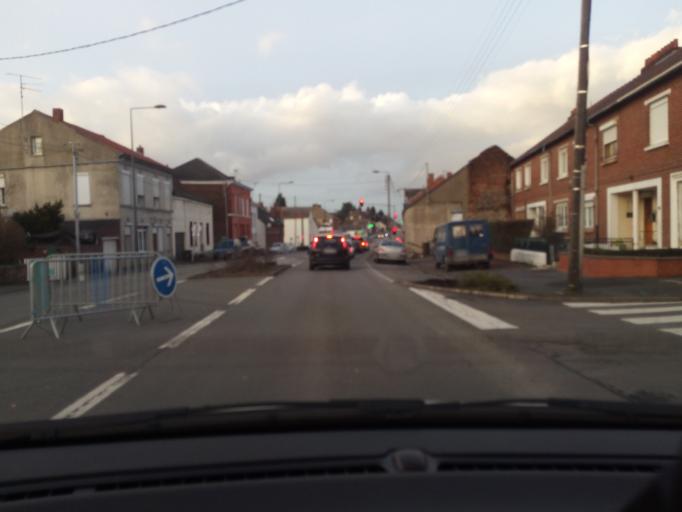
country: FR
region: Nord-Pas-de-Calais
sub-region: Departement du Nord
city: Maubeuge
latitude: 50.2884
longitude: 3.9748
